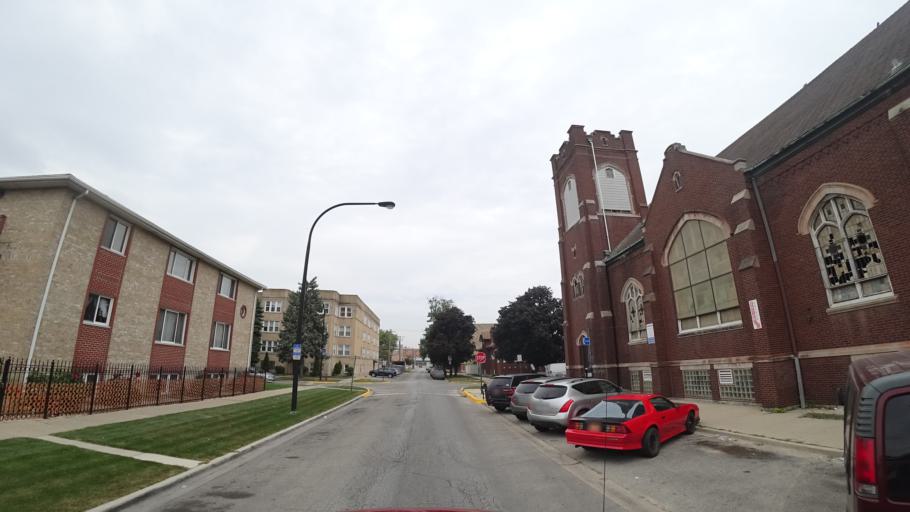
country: US
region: Illinois
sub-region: Cook County
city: Cicero
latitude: 41.8489
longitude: -87.7565
